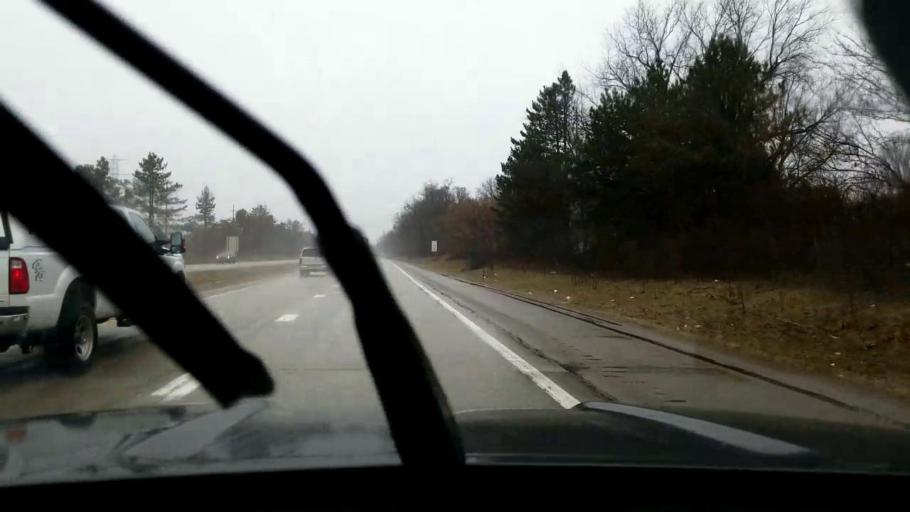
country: US
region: Michigan
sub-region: Jackson County
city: Michigan Center
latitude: 42.2641
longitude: -84.3573
